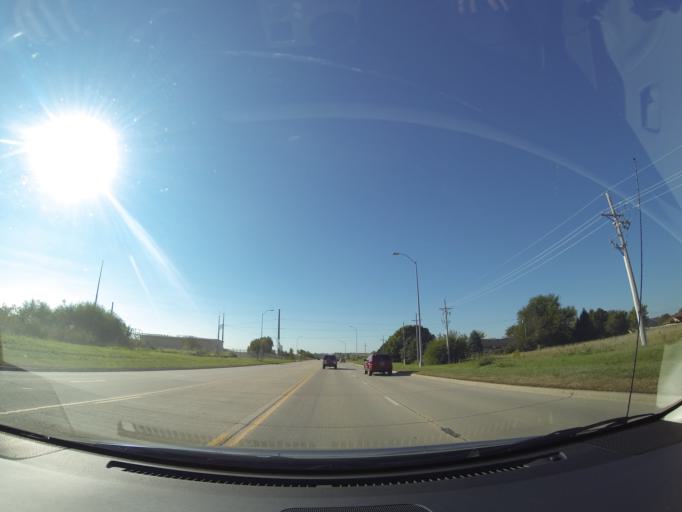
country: US
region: Nebraska
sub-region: Sarpy County
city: Gretna
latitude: 41.1265
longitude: -96.2534
